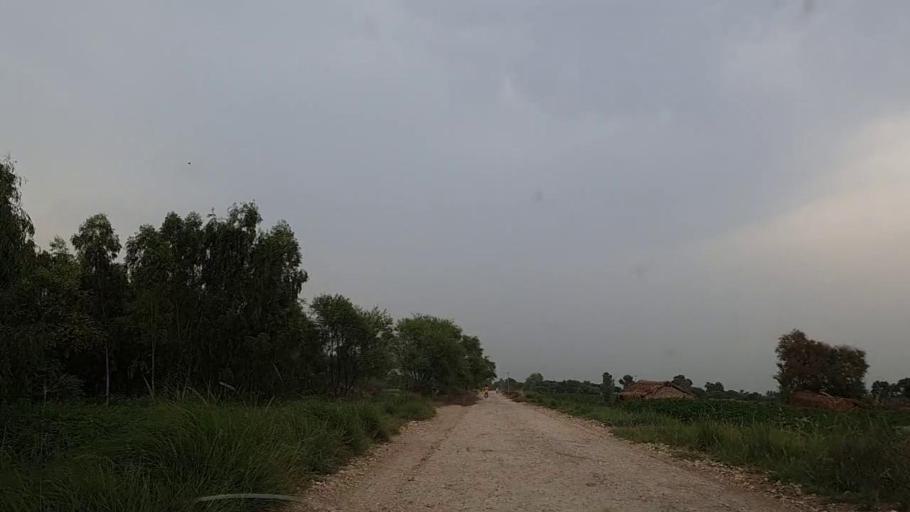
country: PK
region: Sindh
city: Mirpur Mathelo
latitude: 27.8358
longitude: 69.6152
